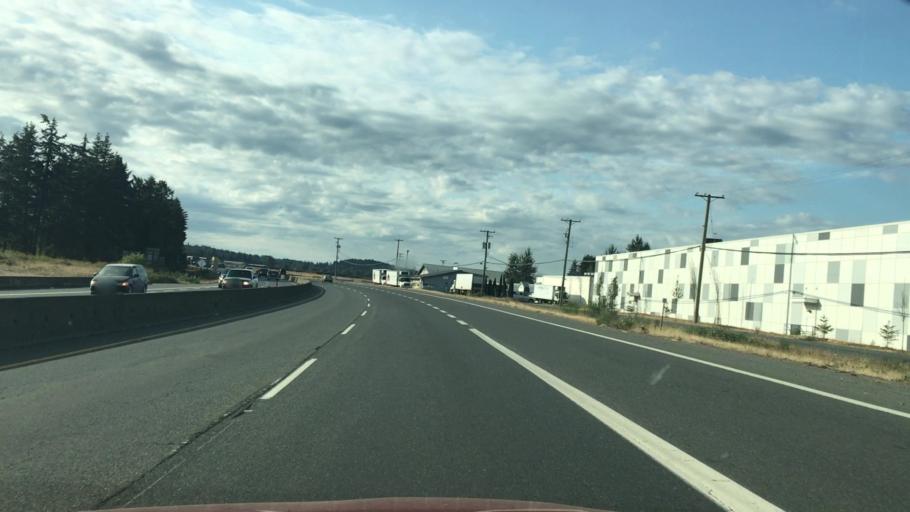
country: CA
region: British Columbia
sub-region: Cowichan Valley Regional District
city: Ladysmith
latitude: 49.0367
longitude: -123.8629
